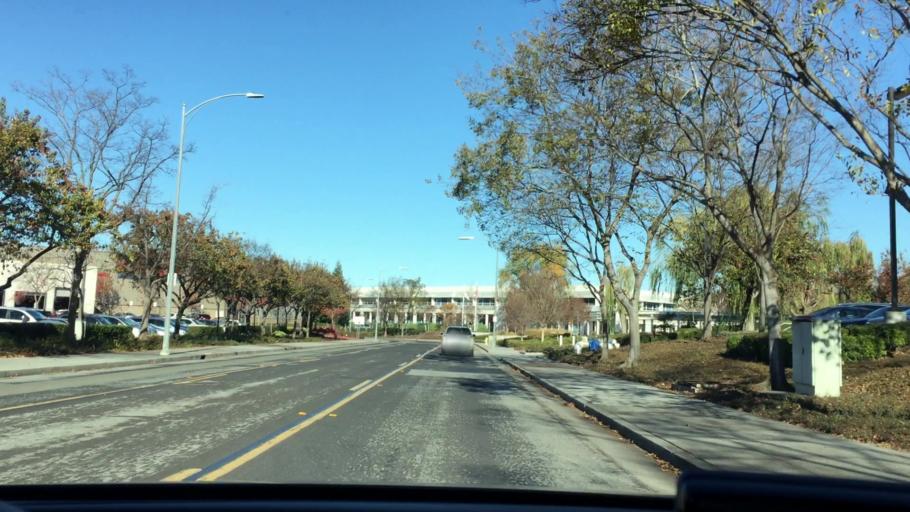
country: US
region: California
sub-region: Santa Clara County
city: Milpitas
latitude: 37.3896
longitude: -121.8832
